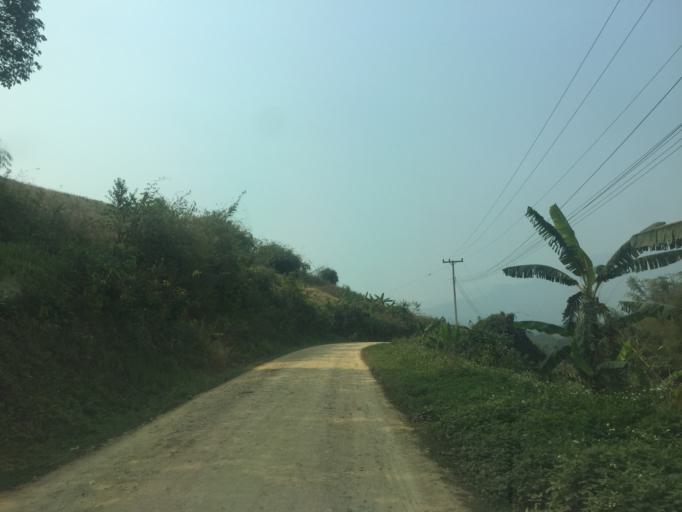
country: TH
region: Phayao
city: Phu Sang
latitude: 19.6565
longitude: 100.5291
